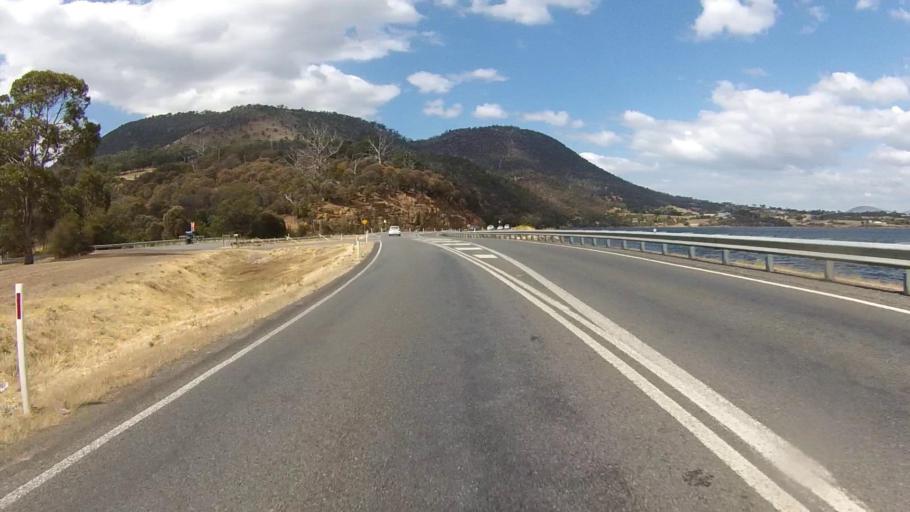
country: AU
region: Tasmania
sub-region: Brighton
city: Old Beach
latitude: -42.7827
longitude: 147.2863
